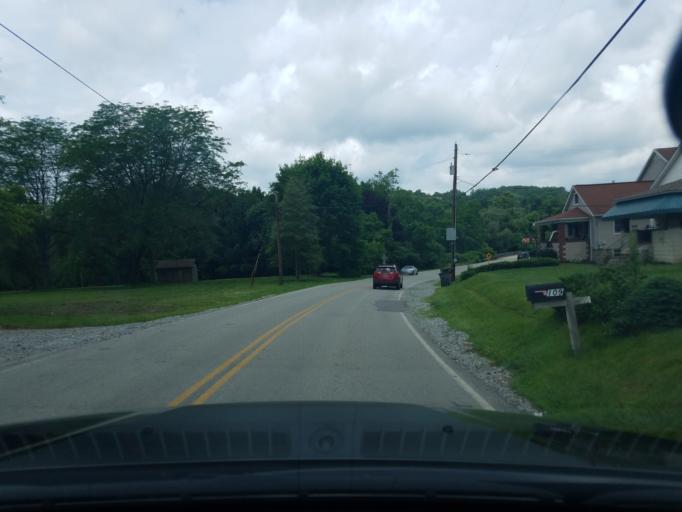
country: US
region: Pennsylvania
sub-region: Westmoreland County
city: Youngwood
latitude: 40.2261
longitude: -79.5879
